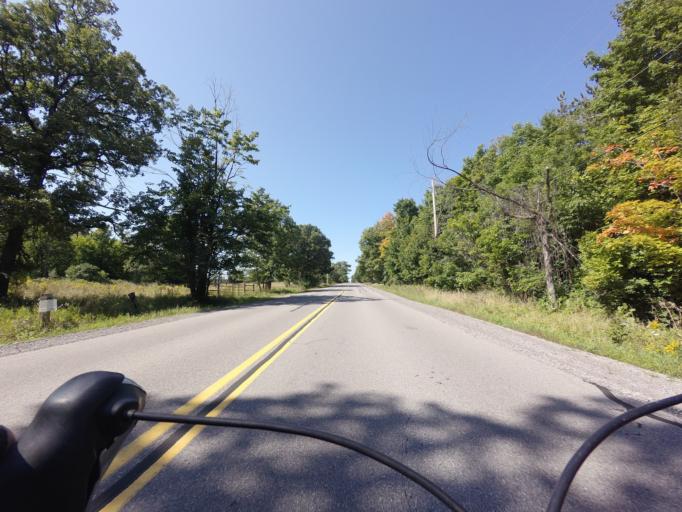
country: CA
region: Ontario
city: Bells Corners
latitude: 45.4082
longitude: -75.9304
